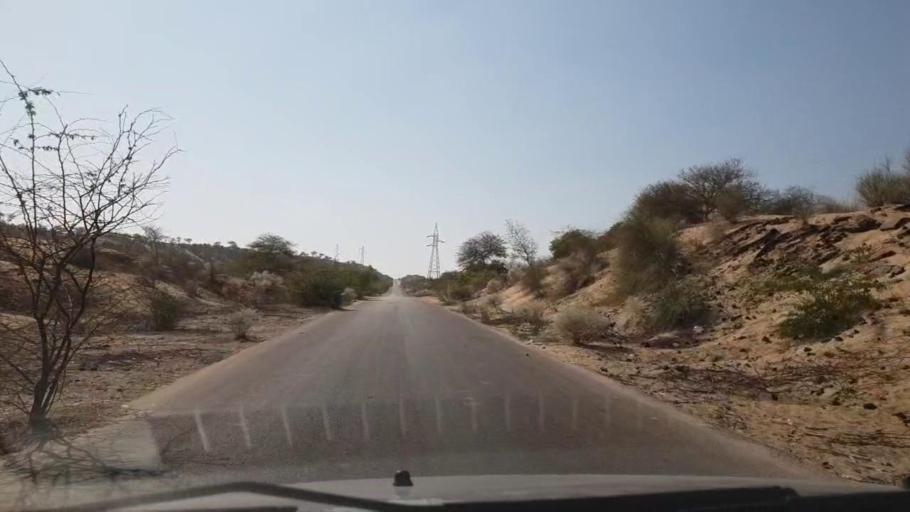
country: PK
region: Sindh
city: Mithi
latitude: 24.6335
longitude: 69.7411
